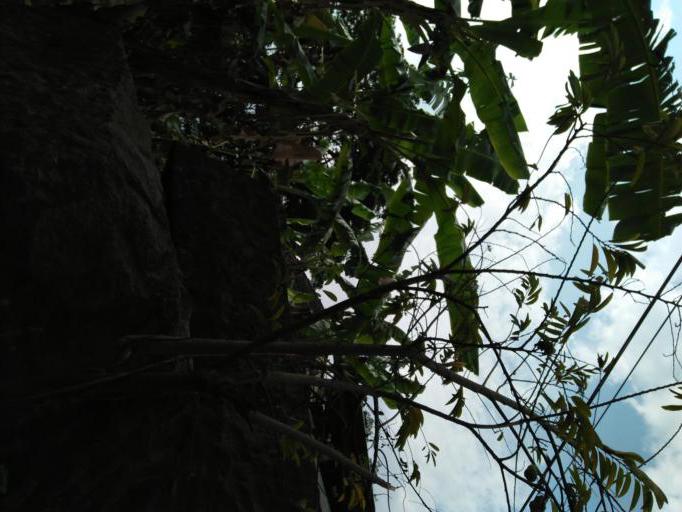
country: ID
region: Central Java
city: Candi Prambanan
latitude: -7.7713
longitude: 110.4815
